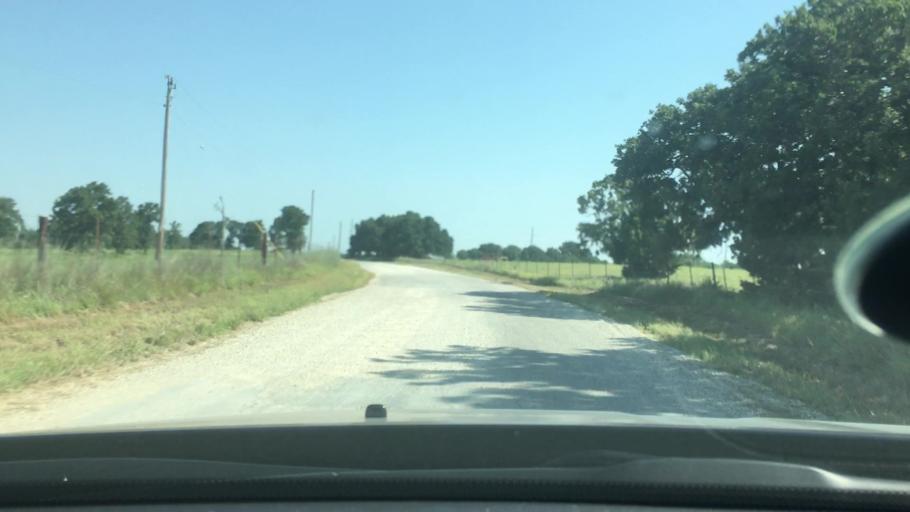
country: US
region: Oklahoma
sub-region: Garvin County
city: Lindsay
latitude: 34.7698
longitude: -97.6123
